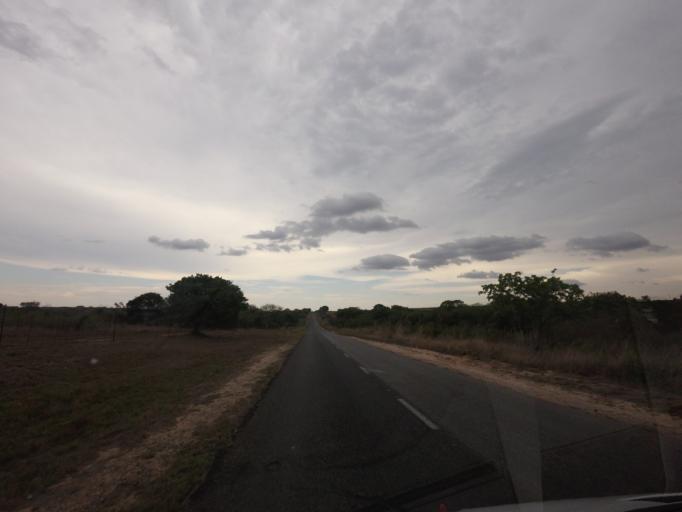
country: ZA
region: Limpopo
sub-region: Mopani District Municipality
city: Hoedspruit
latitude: -24.5376
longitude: 31.0117
